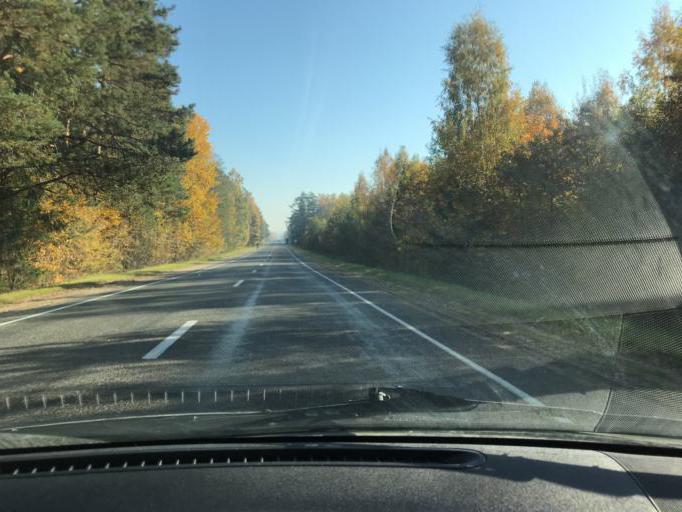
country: BY
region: Brest
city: Lyakhavichy
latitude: 52.9559
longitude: 26.2959
